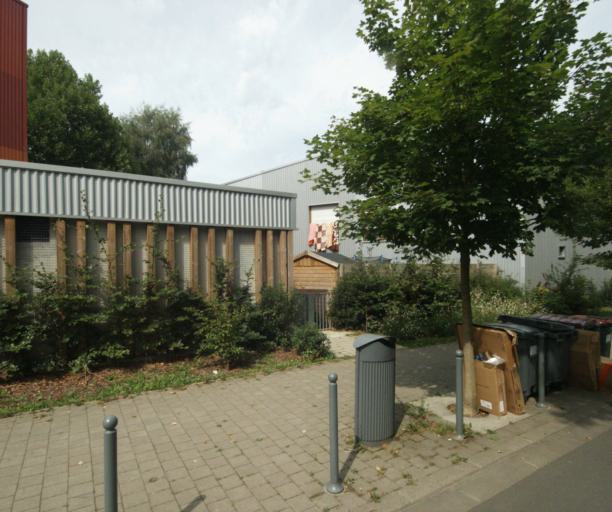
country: FR
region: Nord-Pas-de-Calais
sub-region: Departement du Nord
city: Wattignies
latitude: 50.6028
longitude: 3.0521
